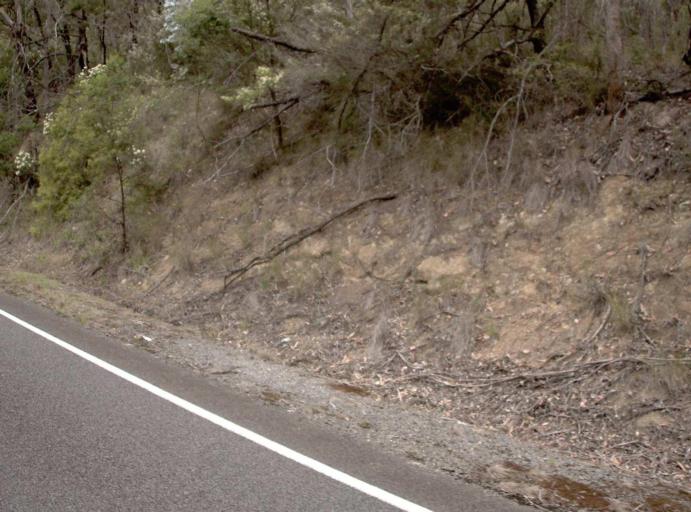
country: AU
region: New South Wales
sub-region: Bombala
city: Bombala
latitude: -37.2663
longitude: 149.2309
